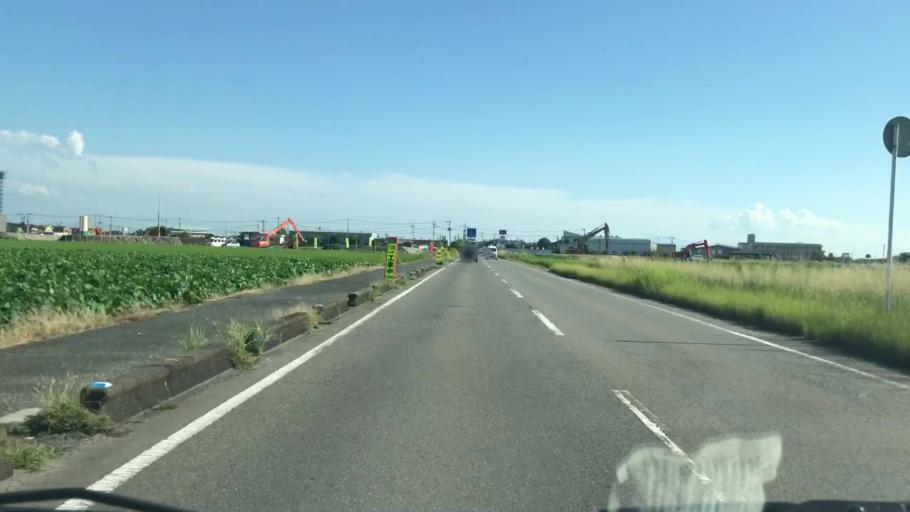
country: JP
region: Saga Prefecture
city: Okawa
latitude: 33.2162
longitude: 130.3349
